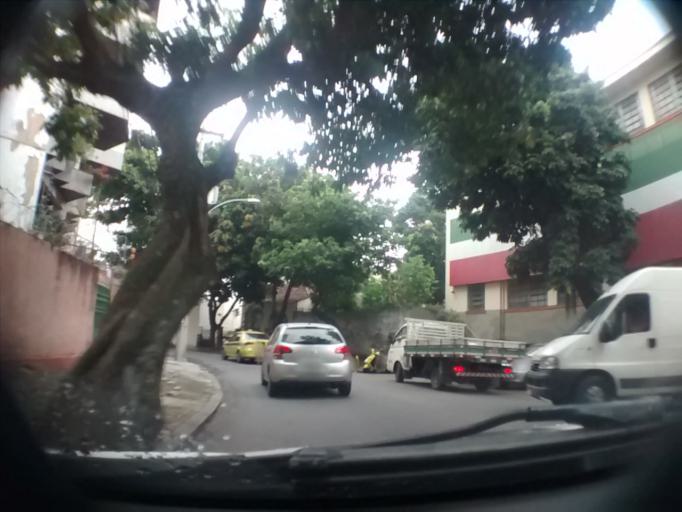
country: BR
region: Rio de Janeiro
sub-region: Rio De Janeiro
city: Rio de Janeiro
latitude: -22.9346
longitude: -43.2459
